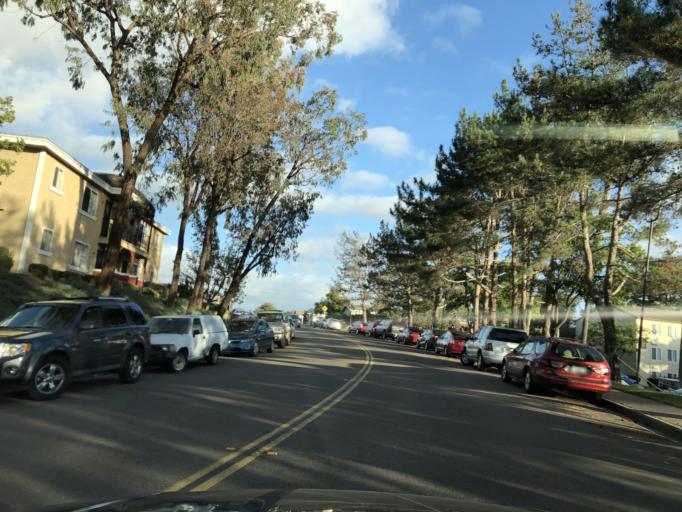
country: US
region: California
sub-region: San Diego County
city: La Jolla
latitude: 32.8171
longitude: -117.1767
